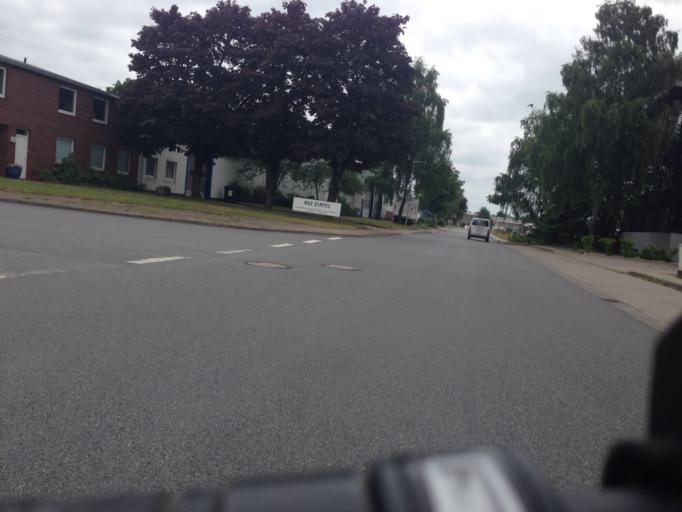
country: DE
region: Schleswig-Holstein
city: Barsbuettel
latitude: 53.5715
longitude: 10.1878
